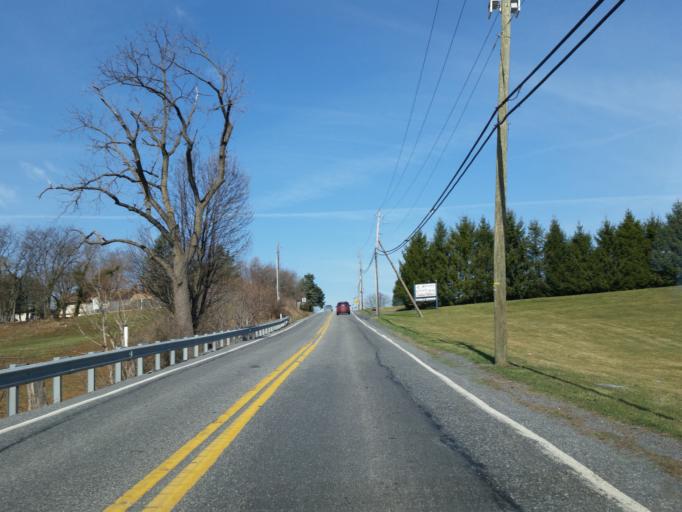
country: US
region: Pennsylvania
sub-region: Lebanon County
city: Avon
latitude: 40.3514
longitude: -76.3890
